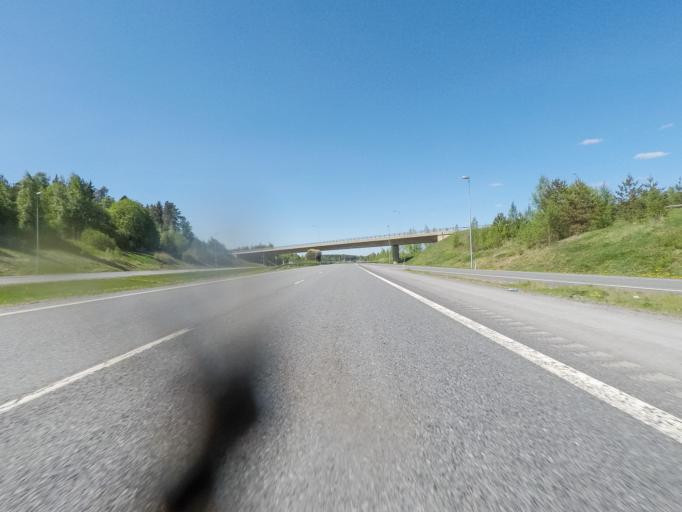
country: FI
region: Pirkanmaa
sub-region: Etelae-Pirkanmaa
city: Akaa
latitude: 61.1596
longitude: 23.9667
